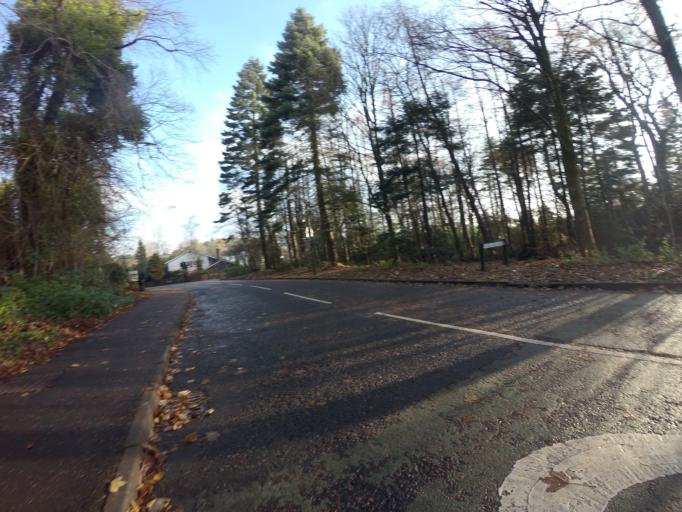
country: GB
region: Scotland
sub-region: West Lothian
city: Livingston
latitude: 55.9088
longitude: -3.5585
